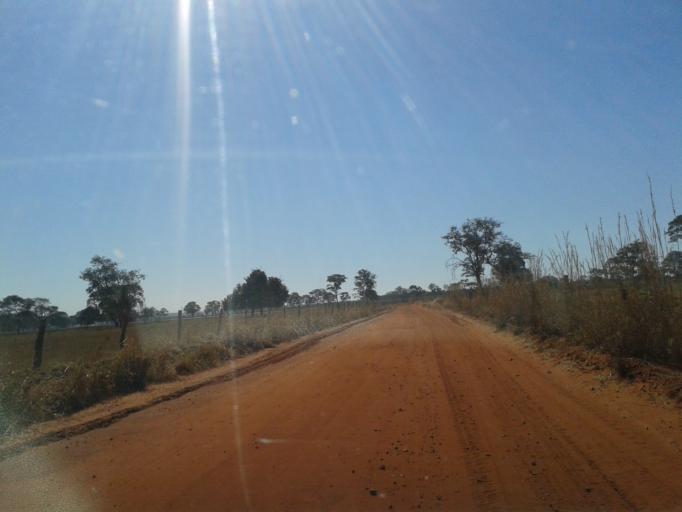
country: BR
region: Minas Gerais
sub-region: Santa Vitoria
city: Santa Vitoria
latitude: -19.0320
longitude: -50.3654
